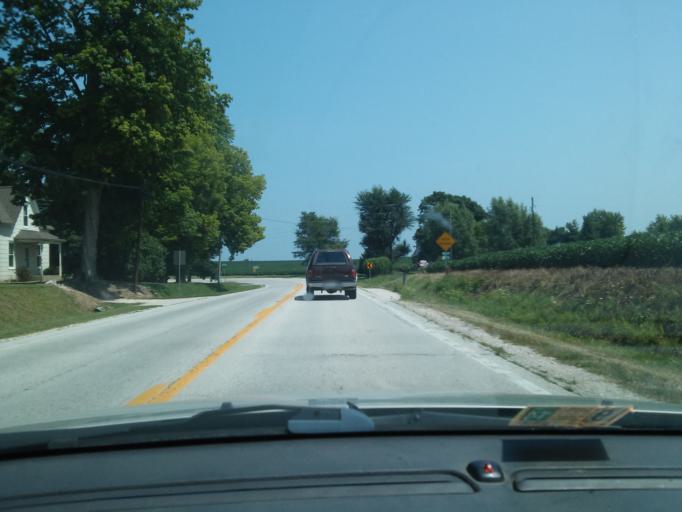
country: US
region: Illinois
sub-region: Pike County
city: Pittsfield
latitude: 39.5478
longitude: -90.9174
